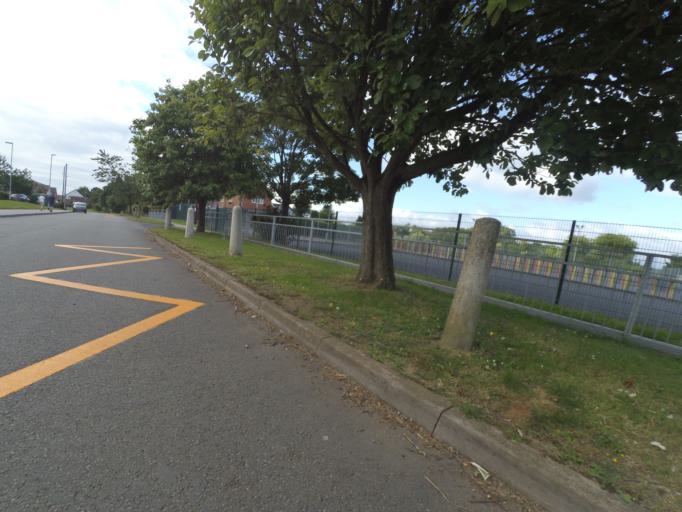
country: GB
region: England
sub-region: Staffordshire
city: Gnosall
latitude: 52.7833
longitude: -2.2516
